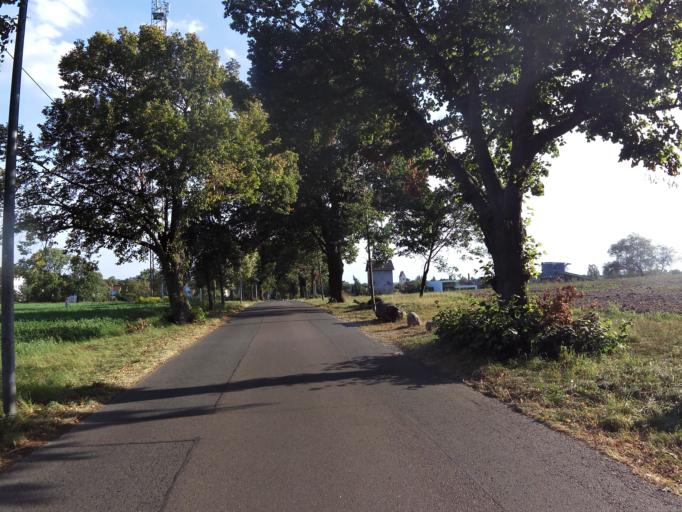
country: DE
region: Saxony
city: Schkeuditz
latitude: 51.3489
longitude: 12.2524
